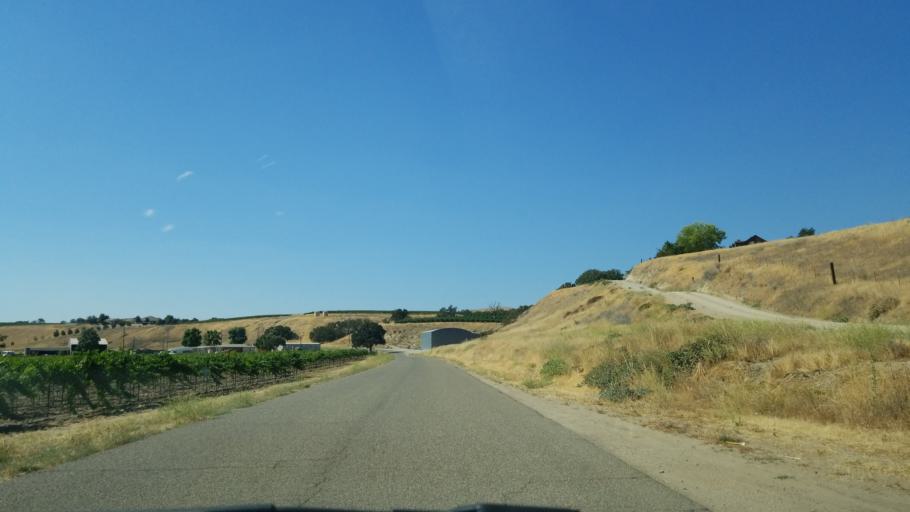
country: US
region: California
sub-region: San Luis Obispo County
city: San Miguel
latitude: 35.7267
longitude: -120.6550
